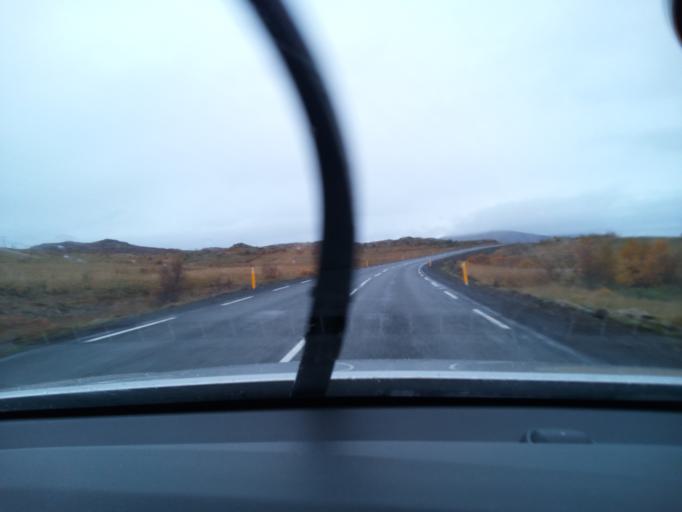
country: IS
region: Capital Region
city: Mosfellsbaer
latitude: 64.3975
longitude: -21.6895
